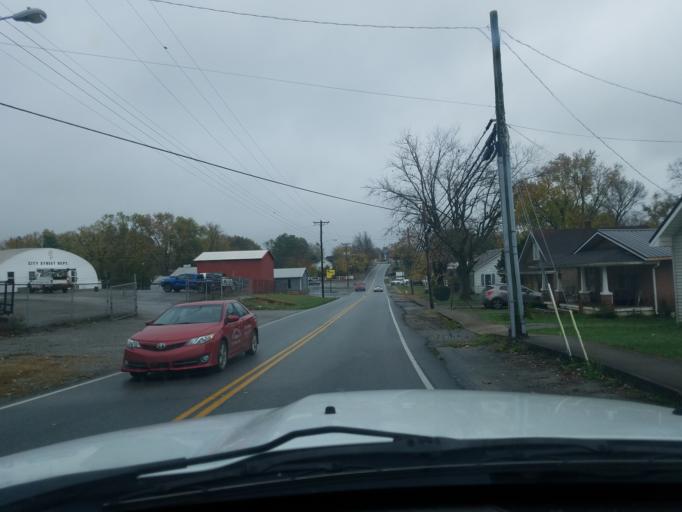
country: US
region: Kentucky
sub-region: Taylor County
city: Campbellsville
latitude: 37.3382
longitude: -85.3382
